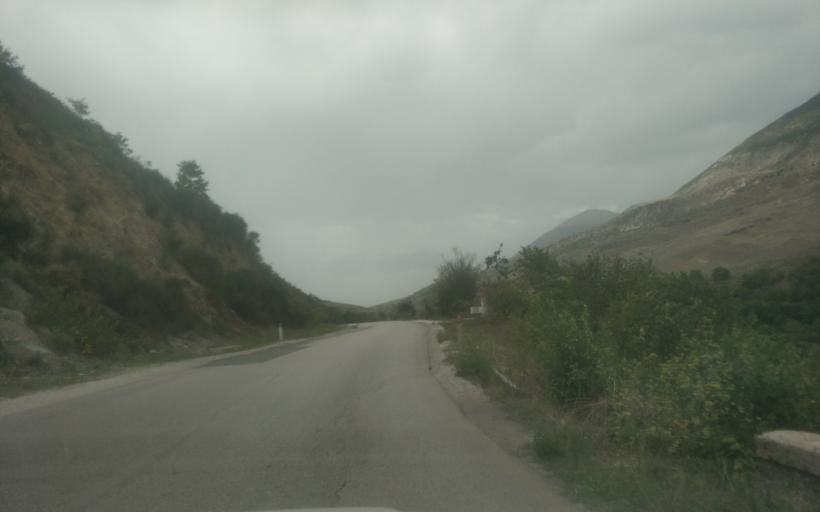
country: AL
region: Gjirokaster
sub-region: Rrethi i Gjirokastres
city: Picar
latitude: 40.2308
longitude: 20.0830
